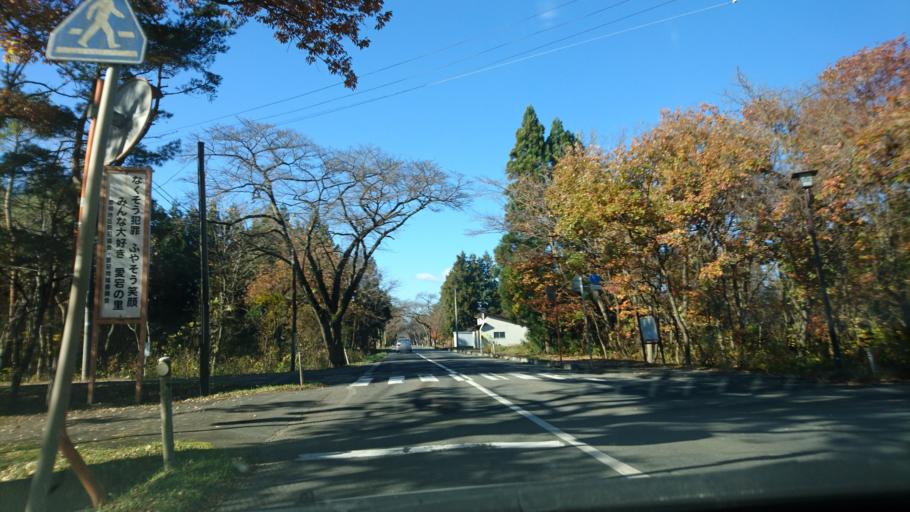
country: JP
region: Iwate
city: Mizusawa
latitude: 39.1266
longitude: 141.0055
